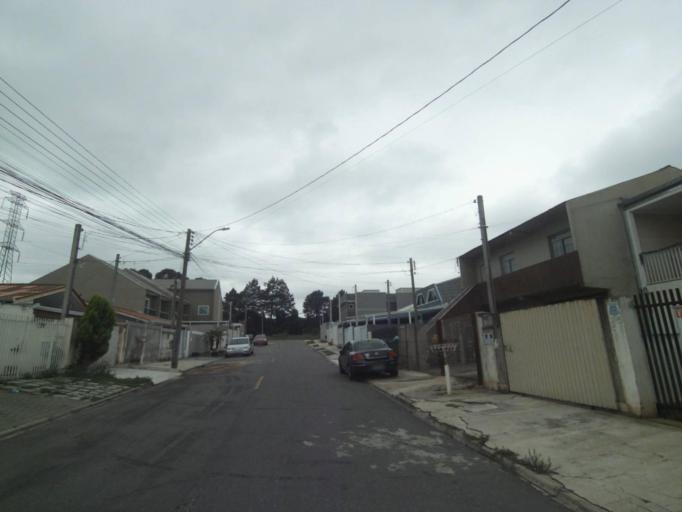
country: BR
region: Parana
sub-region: Araucaria
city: Araucaria
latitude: -25.5469
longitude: -49.3369
